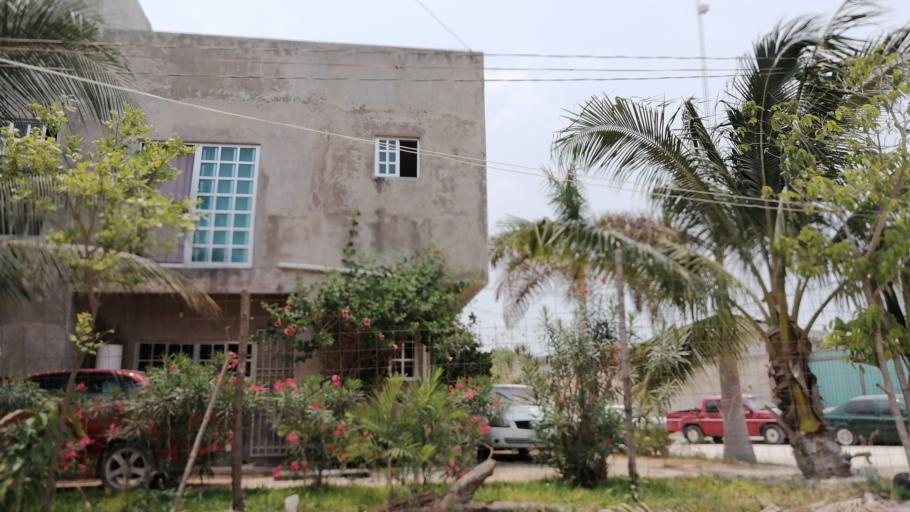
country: MX
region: Quintana Roo
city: Cancun
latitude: 21.1375
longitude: -86.8973
